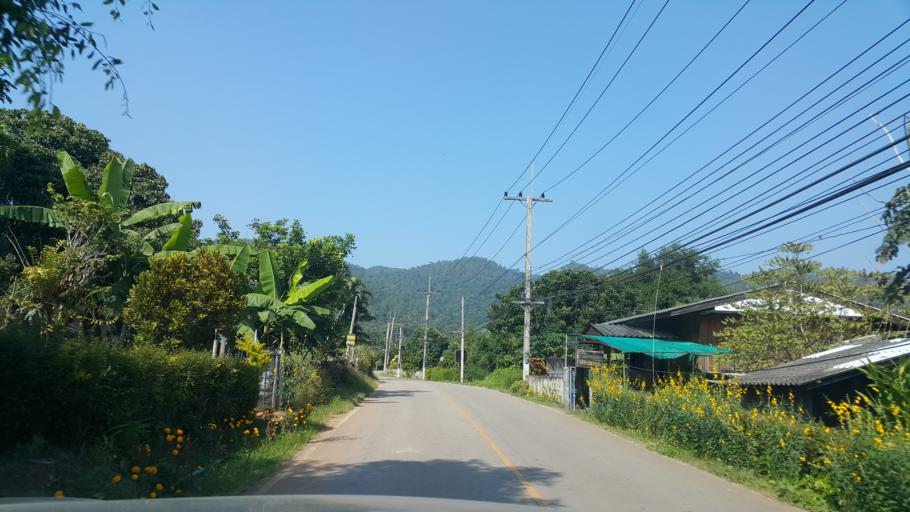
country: TH
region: Chiang Mai
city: Samoeng
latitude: 18.8582
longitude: 98.7017
